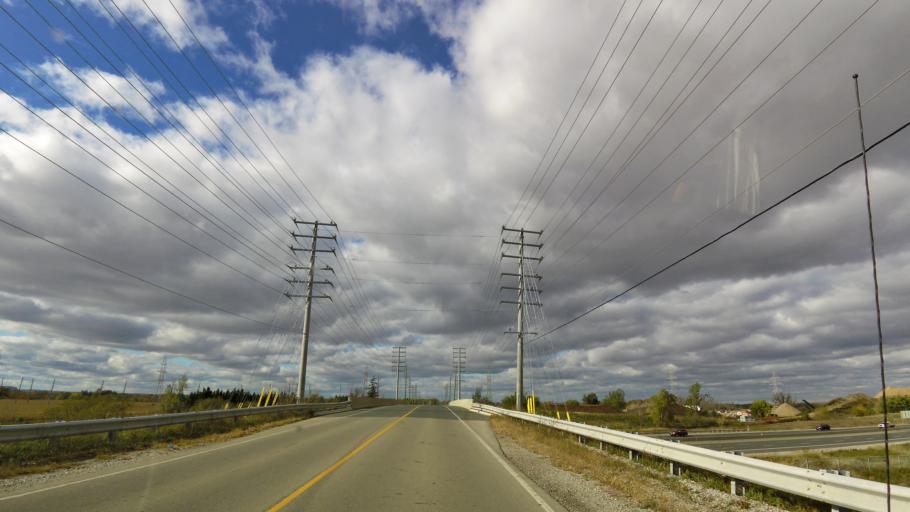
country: CA
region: Ontario
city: Oakville
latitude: 43.4995
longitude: -79.7566
